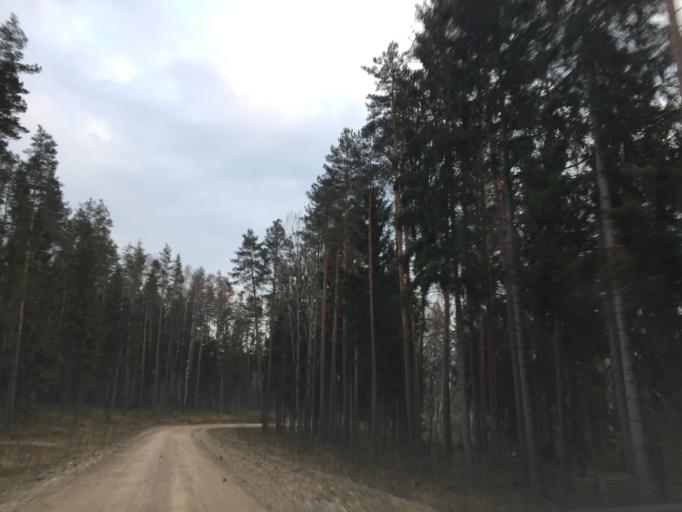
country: LV
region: Raunas
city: Rauna
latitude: 57.1355
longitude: 25.6032
